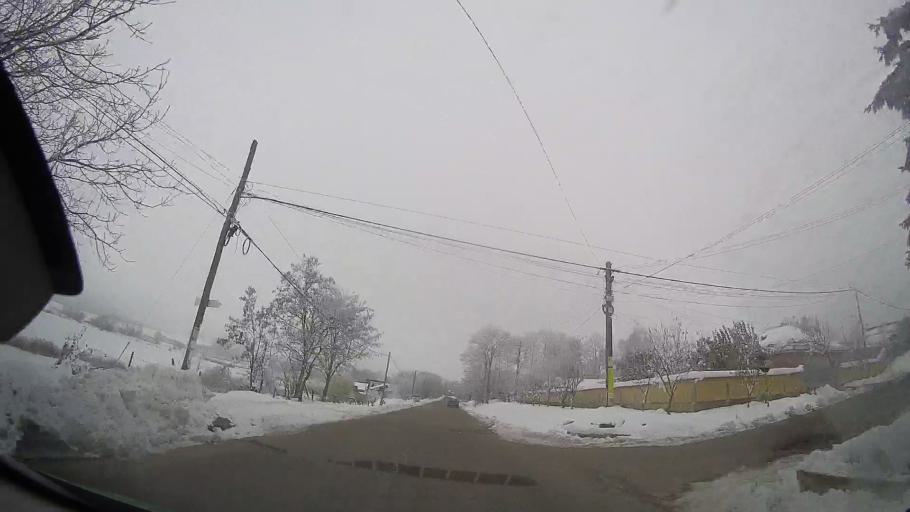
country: RO
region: Neamt
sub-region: Comuna Icusesti
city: Balusesti
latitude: 46.8583
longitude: 27.0233
